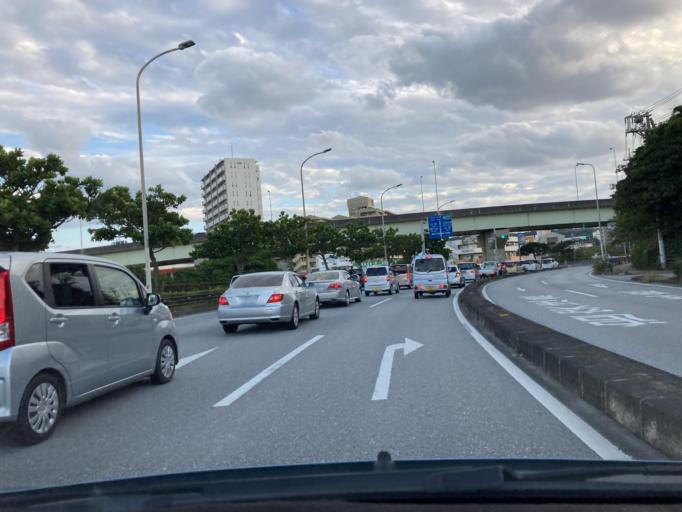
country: JP
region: Okinawa
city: Ginowan
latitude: 26.2683
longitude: 127.7267
